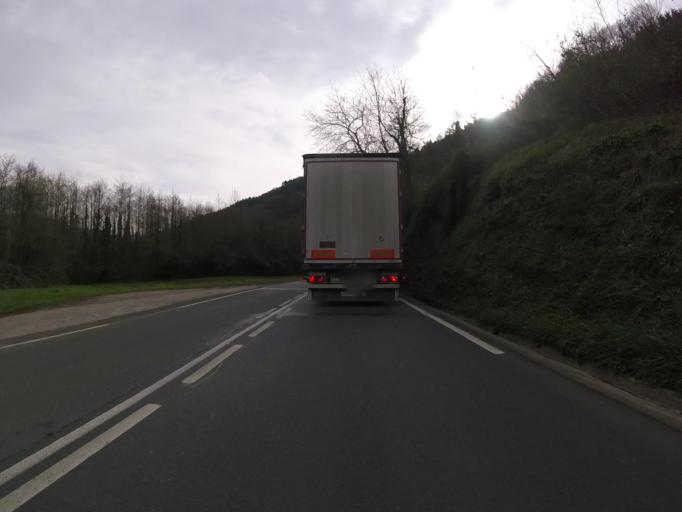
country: ES
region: Basque Country
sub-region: Provincia de Guipuzcoa
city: Cestona
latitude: 43.2537
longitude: -2.2545
